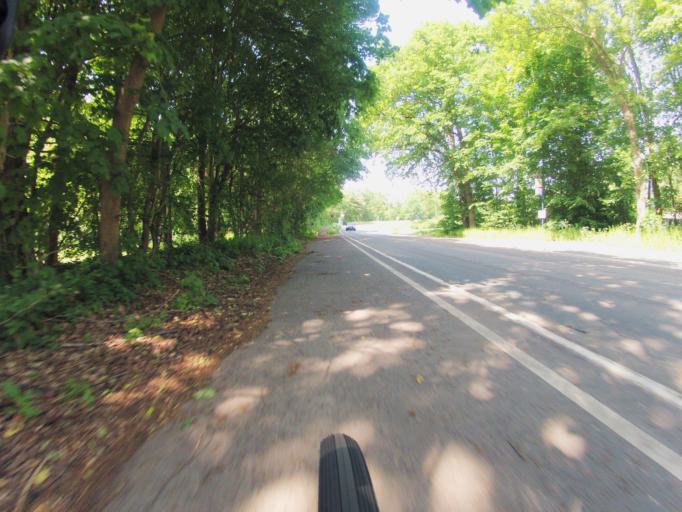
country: DE
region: North Rhine-Westphalia
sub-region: Regierungsbezirk Munster
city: Horstel
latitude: 52.3222
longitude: 7.6264
